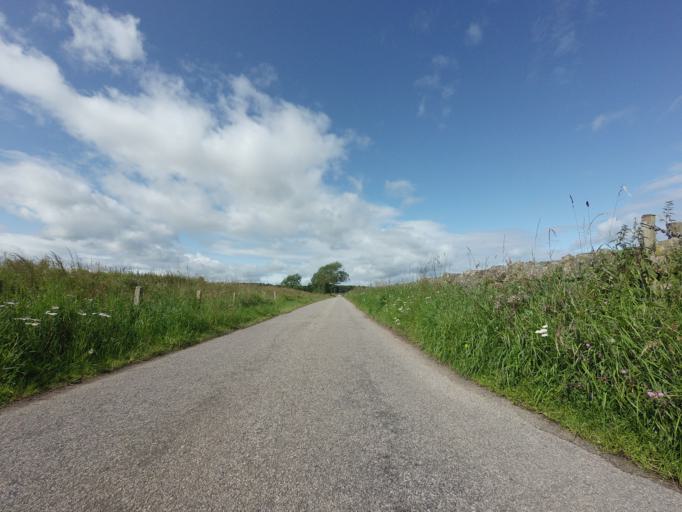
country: GB
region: Scotland
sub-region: Moray
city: Burghead
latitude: 57.6538
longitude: -3.4600
